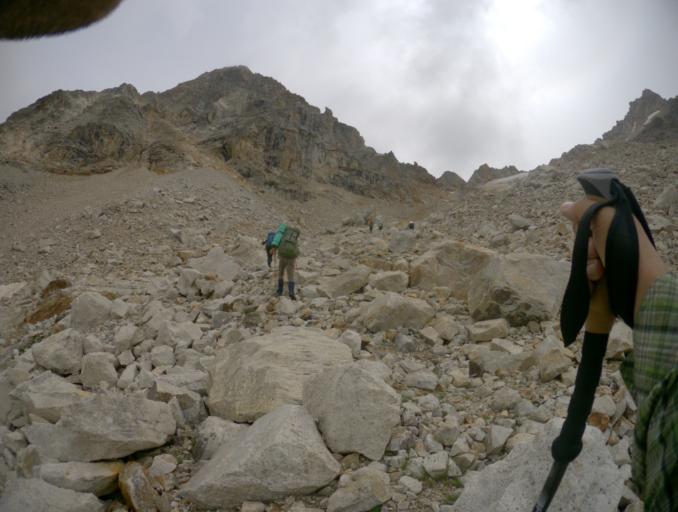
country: RU
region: Karachayevo-Cherkesiya
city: Uchkulan
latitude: 43.2804
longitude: 42.1110
